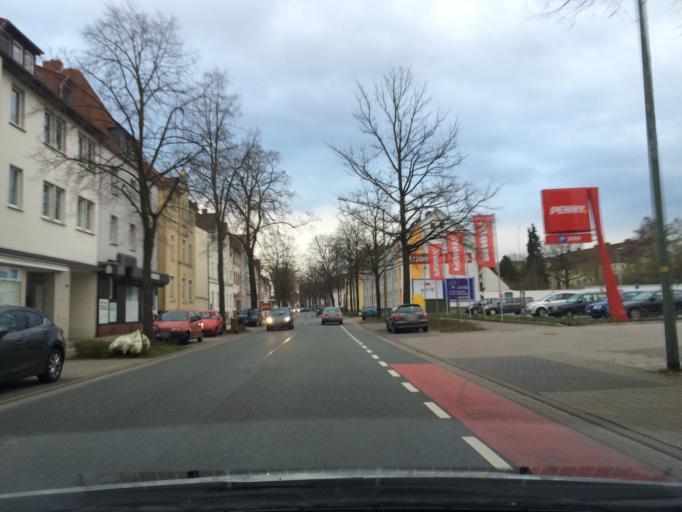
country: DE
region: Lower Saxony
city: Osnabrueck
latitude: 52.2608
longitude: 8.0646
